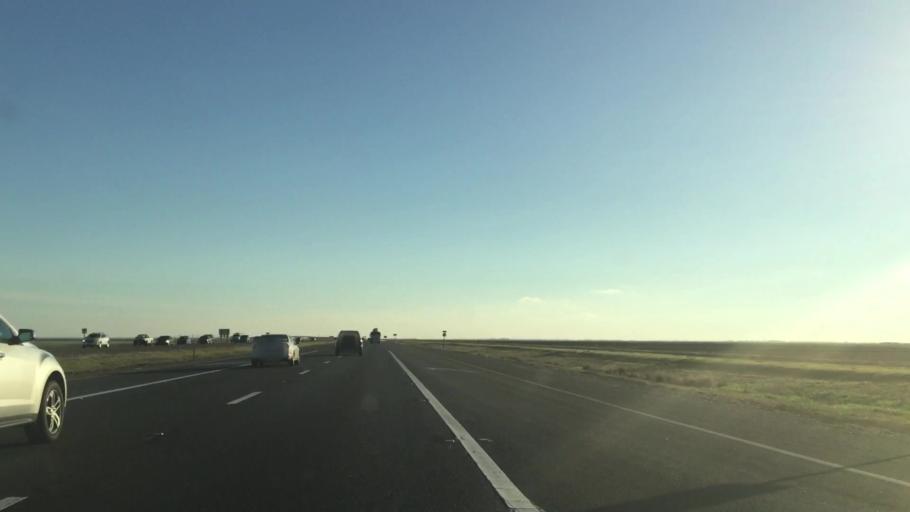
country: US
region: California
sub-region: Sacramento County
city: Elverta
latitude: 38.7791
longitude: -121.5438
